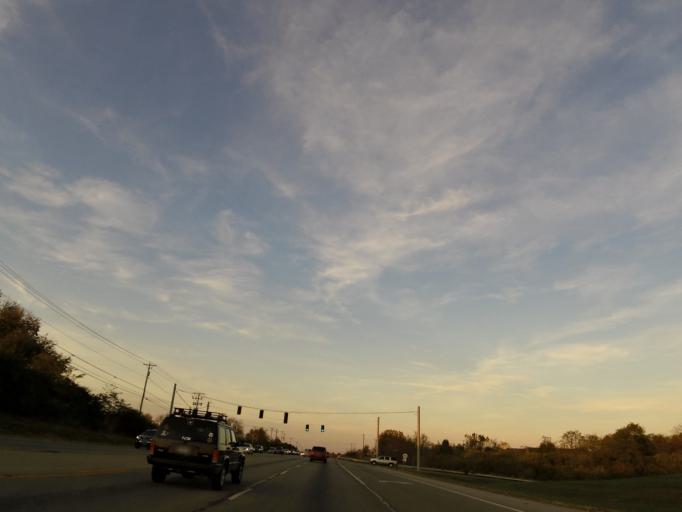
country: US
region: Kentucky
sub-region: Fayette County
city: Monticello
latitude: 37.9513
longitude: -84.5415
